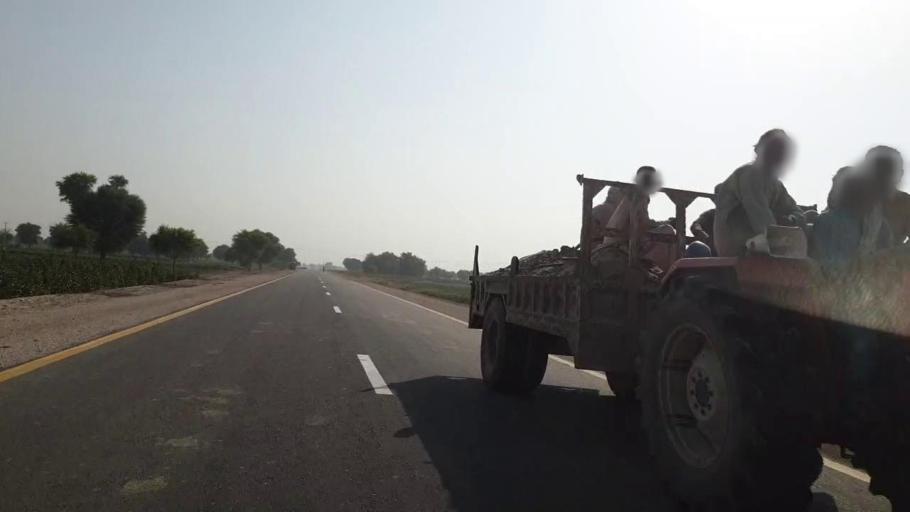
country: PK
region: Sindh
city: Bhan
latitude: 26.5220
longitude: 67.7883
